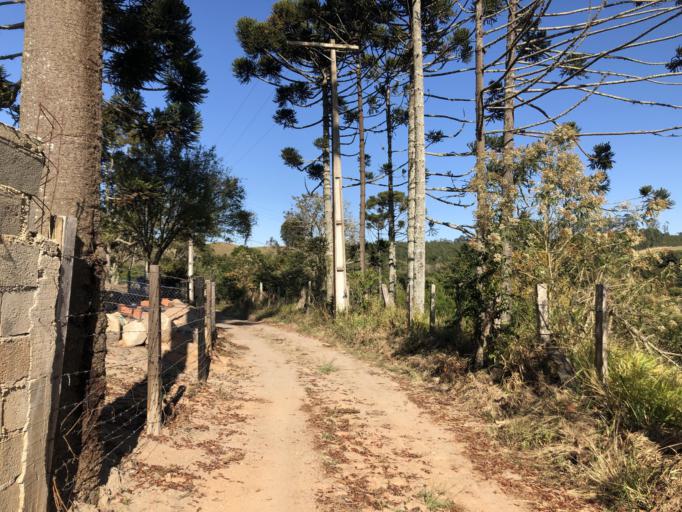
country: BR
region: Sao Paulo
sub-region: Pilar Do Sul
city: Pilar do Sul
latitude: -23.8297
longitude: -47.6262
